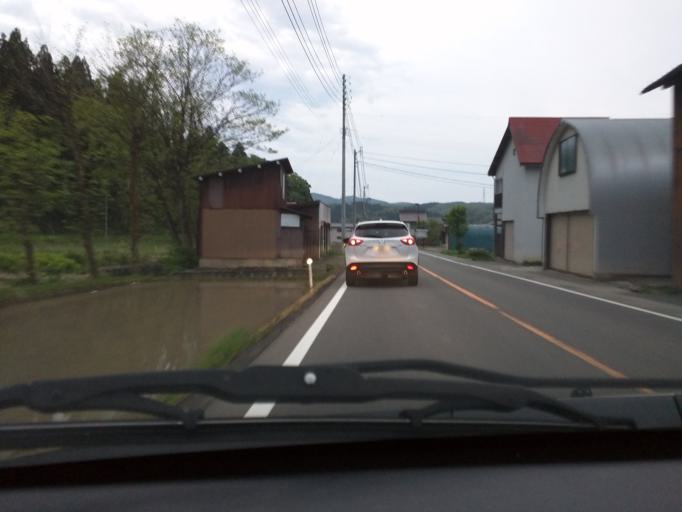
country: JP
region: Niigata
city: Ojiya
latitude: 37.3188
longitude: 138.7217
